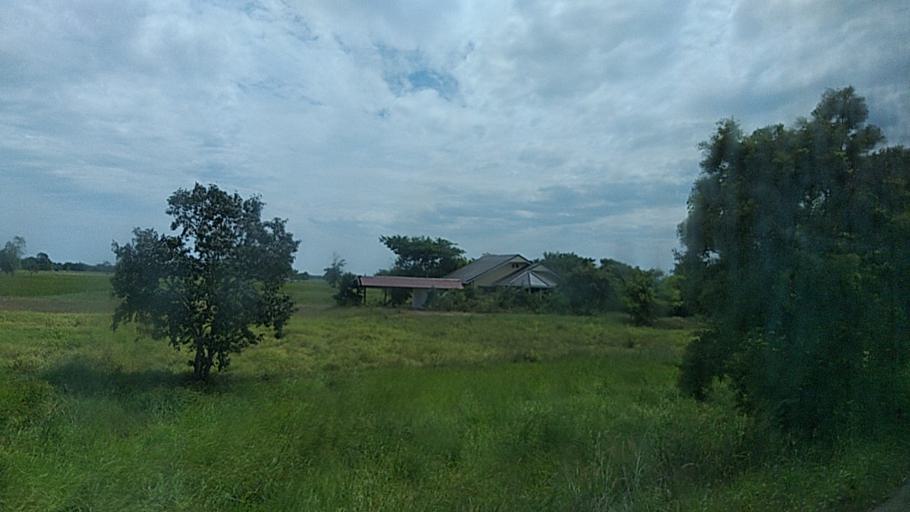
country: TH
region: Maha Sarakham
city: Chiang Yuen
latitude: 16.3743
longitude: 103.1051
